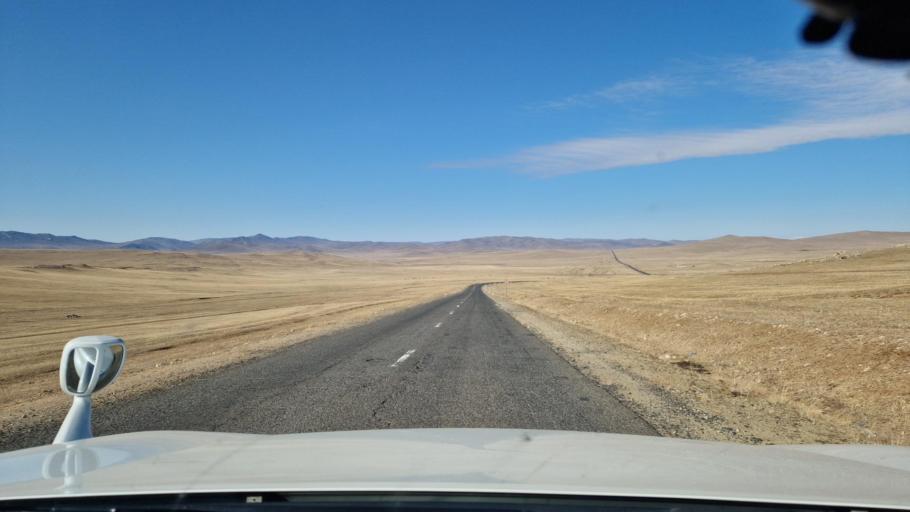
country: MN
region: Hentiy
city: Modot
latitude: 47.5913
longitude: 109.2642
